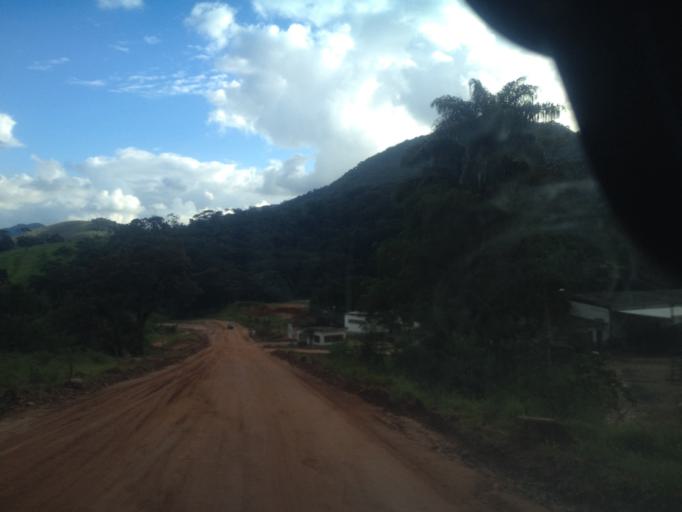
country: BR
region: Rio de Janeiro
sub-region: Quatis
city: Quatis
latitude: -22.2155
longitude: -44.2470
